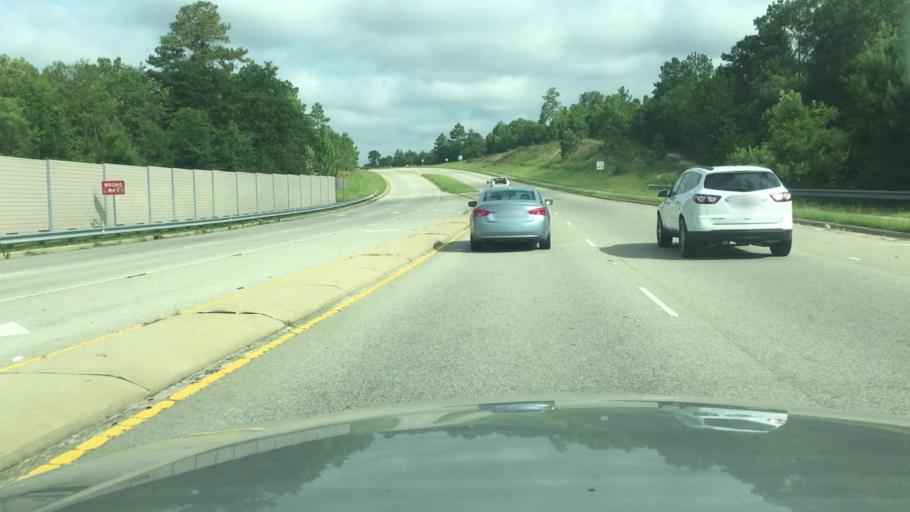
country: US
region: North Carolina
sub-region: Cumberland County
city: Hope Mills
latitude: 34.9870
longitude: -78.9343
